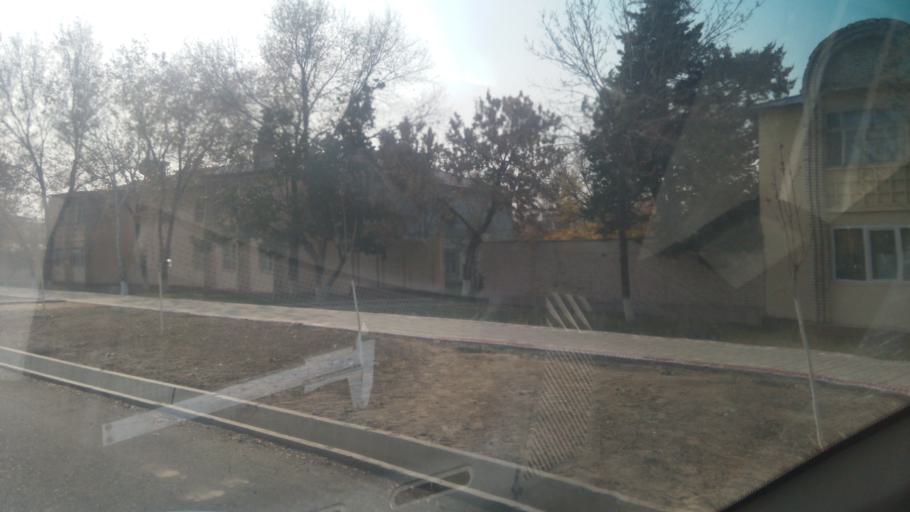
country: UZ
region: Sirdaryo
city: Guliston
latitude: 40.5095
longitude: 68.7730
